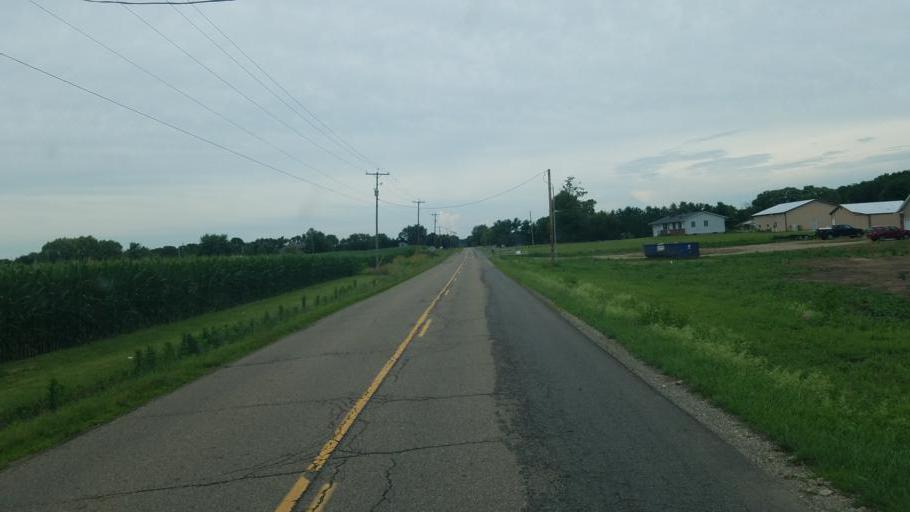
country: US
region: Ohio
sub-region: Knox County
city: Centerburg
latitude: 40.2797
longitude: -82.6902
